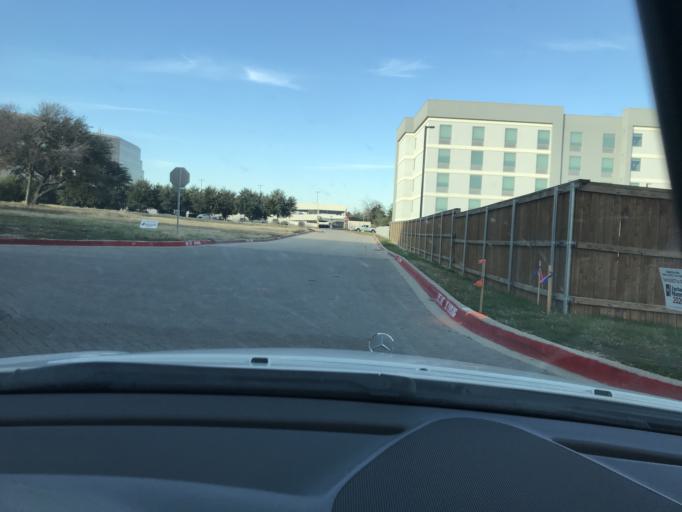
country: US
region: Texas
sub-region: Dallas County
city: University Park
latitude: 32.8905
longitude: -96.7674
